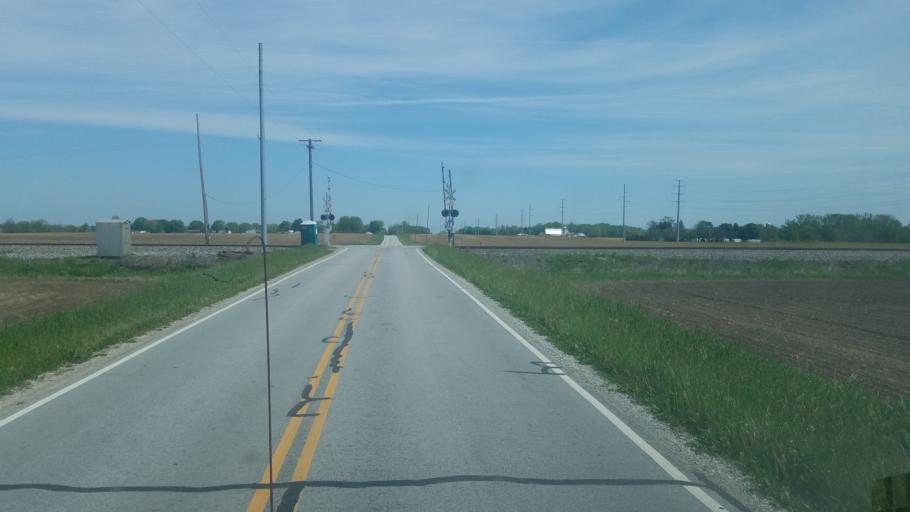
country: US
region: Ohio
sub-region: Seneca County
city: Tiffin
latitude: 41.1151
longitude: -83.1311
